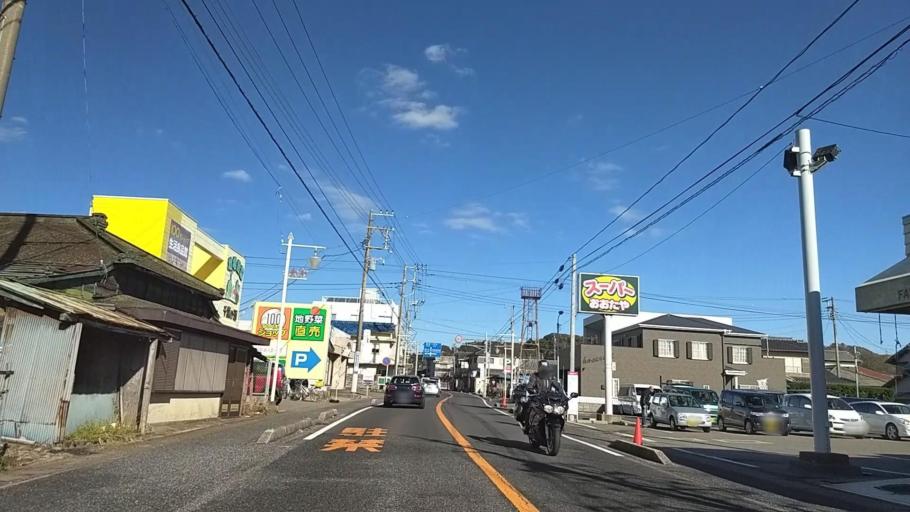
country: JP
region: Chiba
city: Katsuura
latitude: 35.1882
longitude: 140.3570
